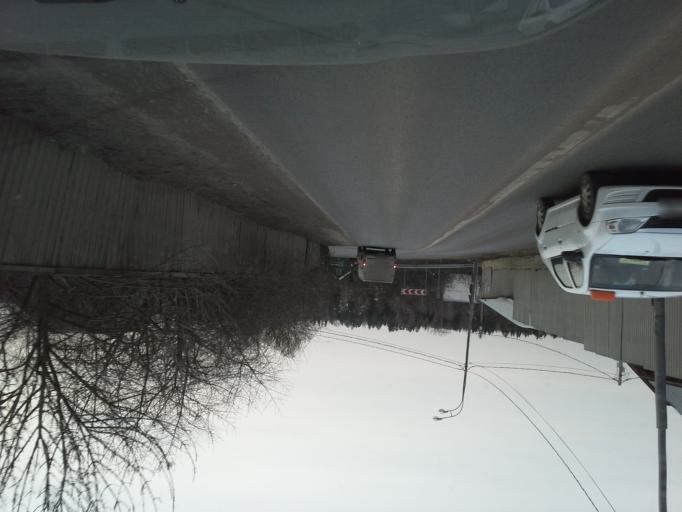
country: RU
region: Moskovskaya
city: Lesnoy Gorodok
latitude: 55.6496
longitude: 37.2109
